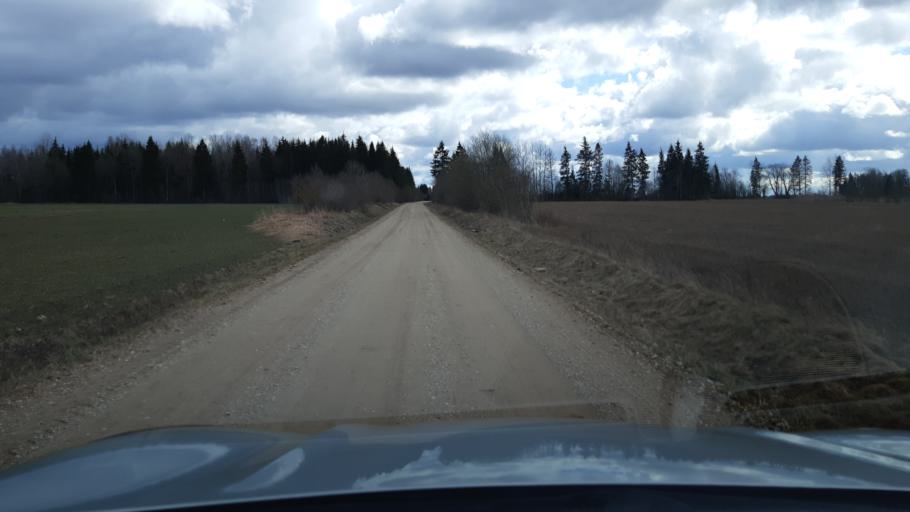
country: EE
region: Harju
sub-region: Rae vald
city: Vaida
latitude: 59.0828
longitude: 25.1428
